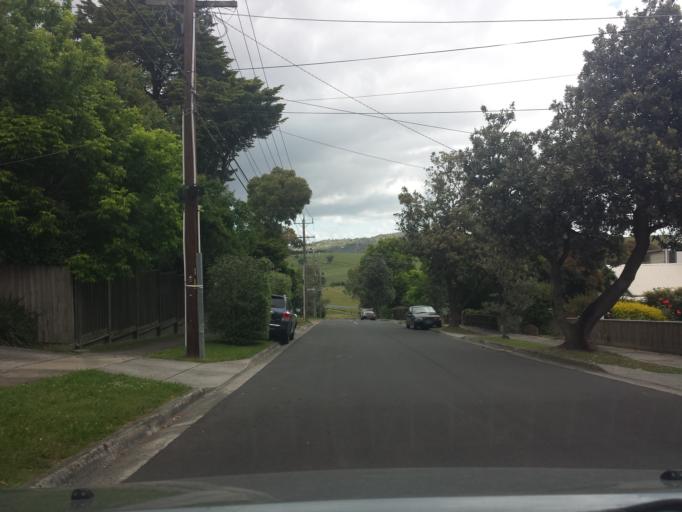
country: AU
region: Victoria
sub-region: Knox
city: Ferntree Gully
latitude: -37.8988
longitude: 145.2930
